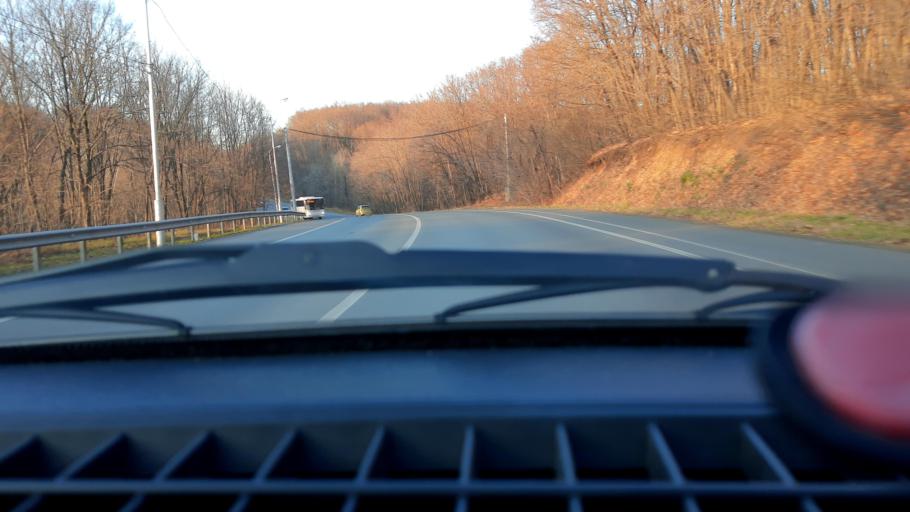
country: RU
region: Bashkortostan
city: Ufa
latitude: 54.8775
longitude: 56.0624
